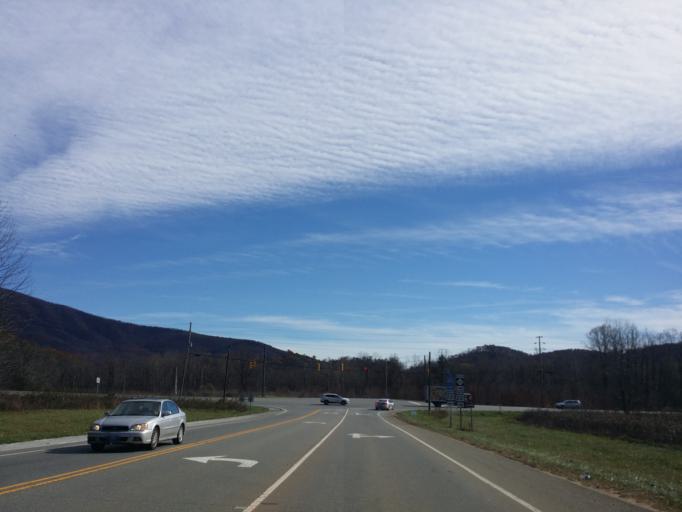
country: US
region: North Carolina
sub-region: McDowell County
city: Marion
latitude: 35.7987
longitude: -82.0343
